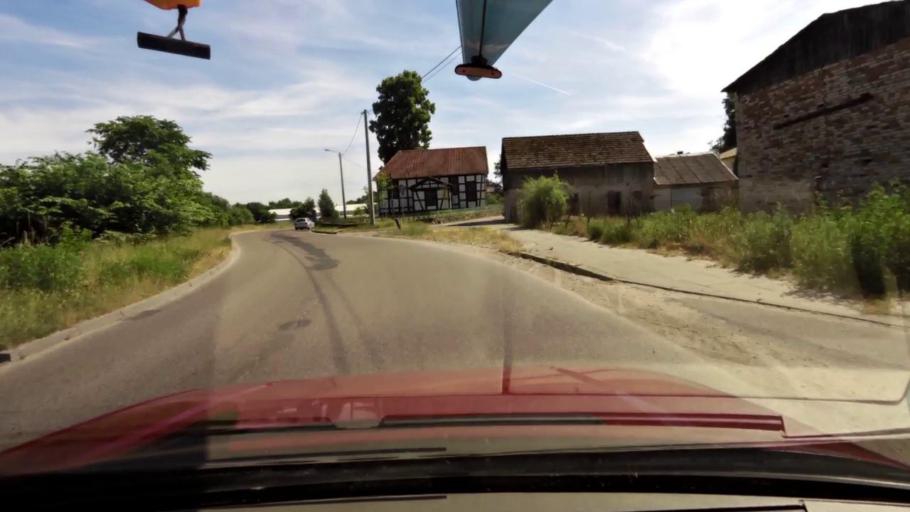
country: PL
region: Pomeranian Voivodeship
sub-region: Powiat slupski
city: Kobylnica
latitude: 54.3541
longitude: 16.9680
